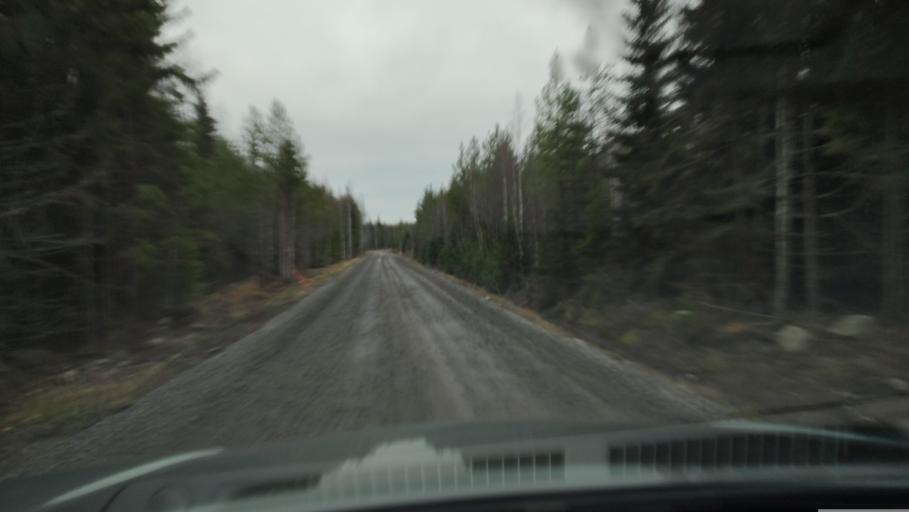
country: FI
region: Southern Ostrobothnia
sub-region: Suupohja
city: Karijoki
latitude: 62.1963
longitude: 21.5751
